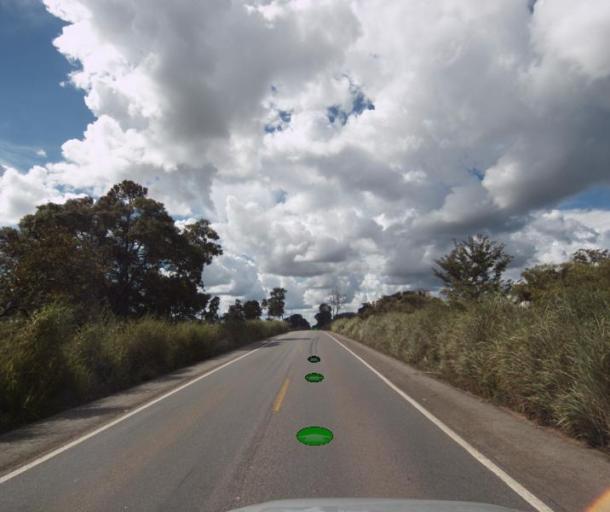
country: BR
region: Goias
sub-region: Porangatu
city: Porangatu
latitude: -13.3760
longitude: -49.1266
